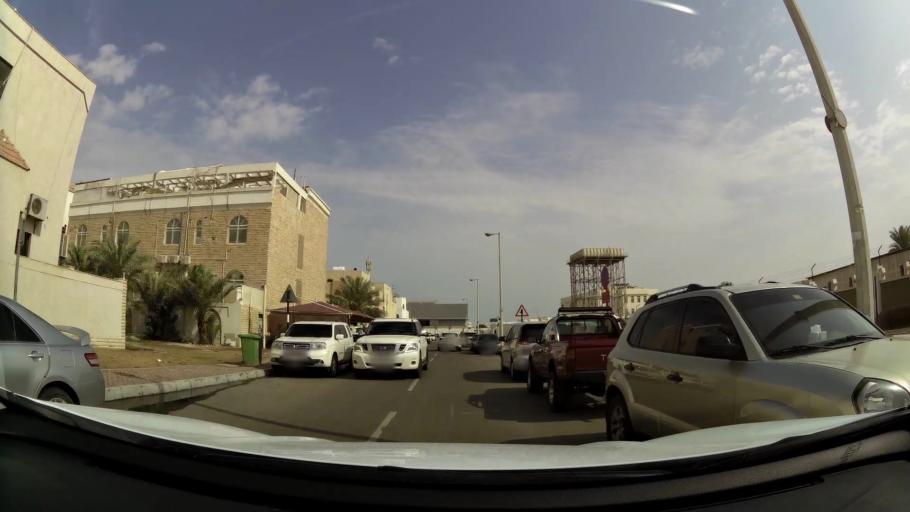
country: AE
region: Abu Dhabi
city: Abu Dhabi
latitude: 24.4388
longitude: 54.4195
